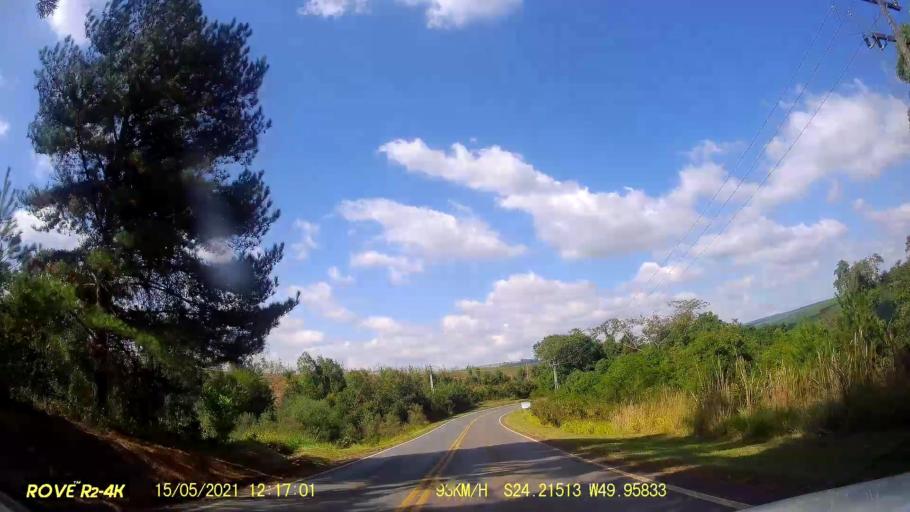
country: BR
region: Parana
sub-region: Jaguariaiva
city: Jaguariaiva
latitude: -24.2151
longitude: -49.9584
